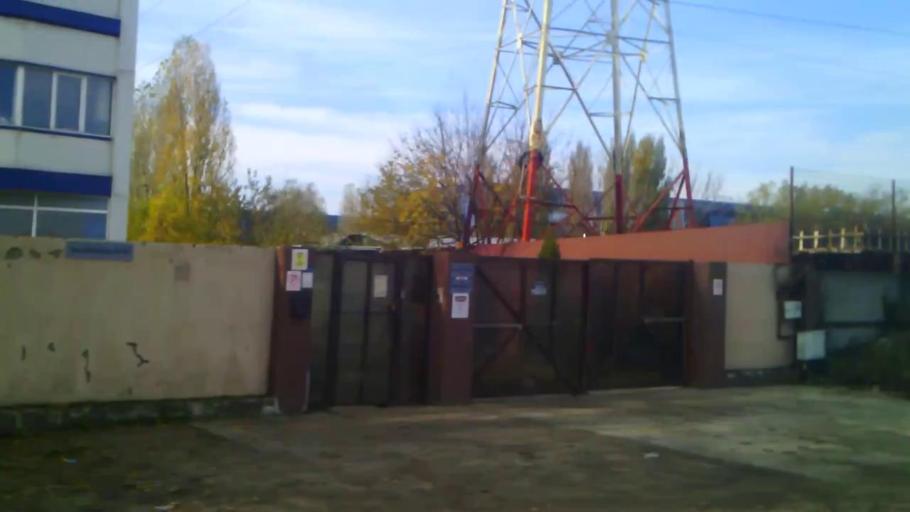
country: RO
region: Ilfov
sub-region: Comuna Popesti-Leordeni
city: Popesti-Leordeni
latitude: 44.3555
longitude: 26.1532
